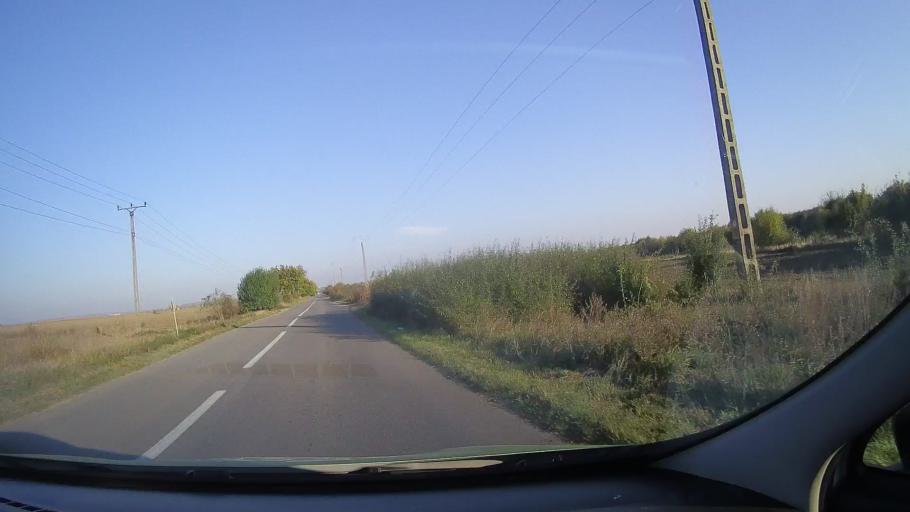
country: RO
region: Bihor
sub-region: Comuna Bors
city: Santion
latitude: 47.1155
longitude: 21.8359
